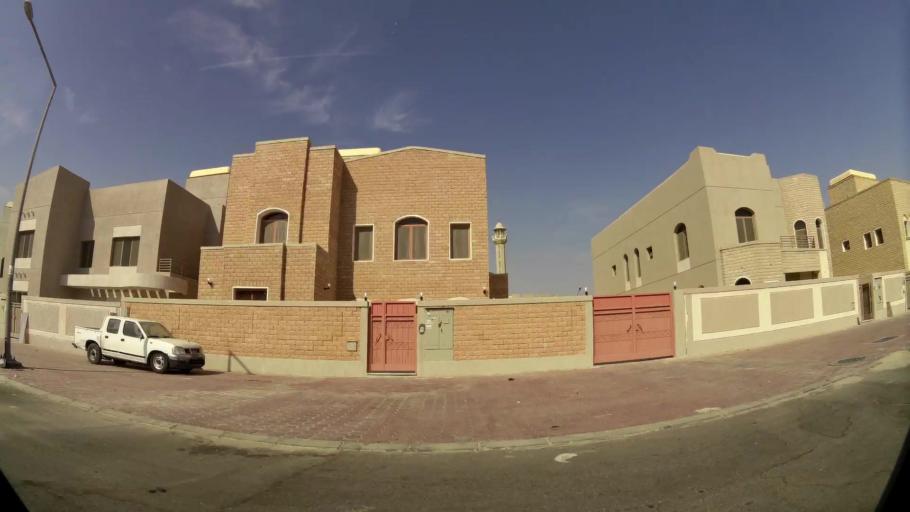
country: KW
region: Al Ahmadi
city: Al Wafrah
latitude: 28.7944
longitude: 48.0754
